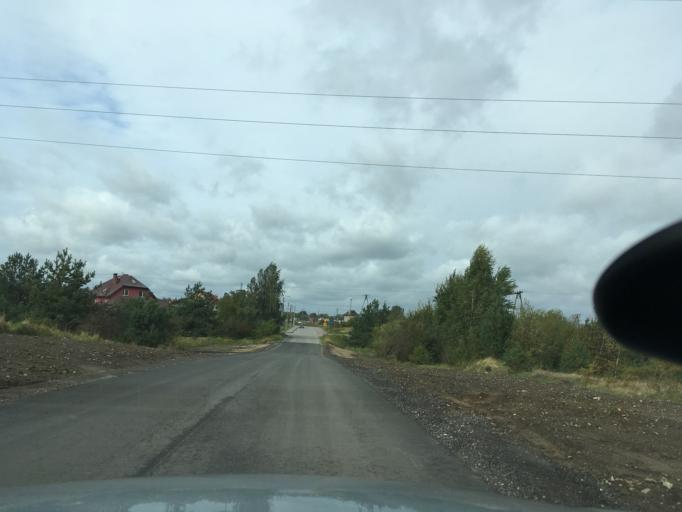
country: PL
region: Pomeranian Voivodeship
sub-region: Powiat koscierski
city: Koscierzyna
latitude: 54.1140
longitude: 18.0056
